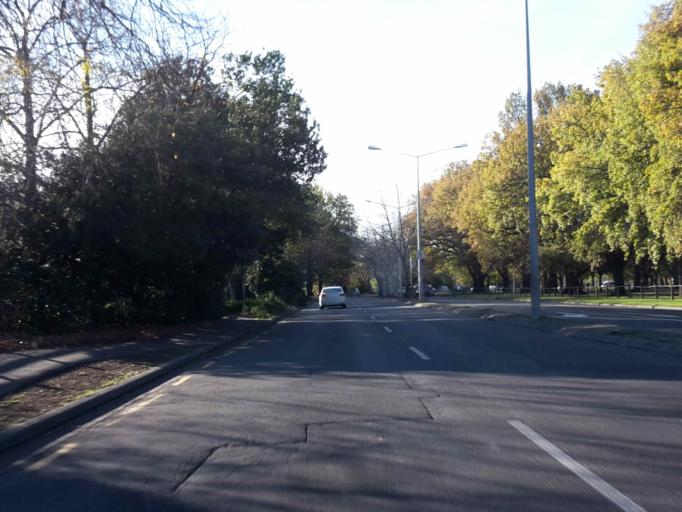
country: NZ
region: Canterbury
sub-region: Christchurch City
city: Christchurch
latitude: -43.5265
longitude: 172.6124
